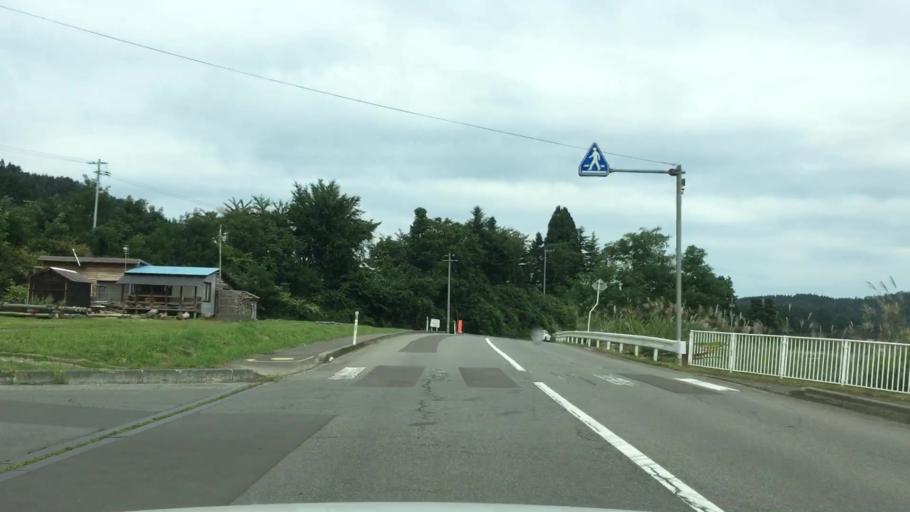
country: JP
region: Aomori
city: Shimokizukuri
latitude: 40.7506
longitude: 140.2293
